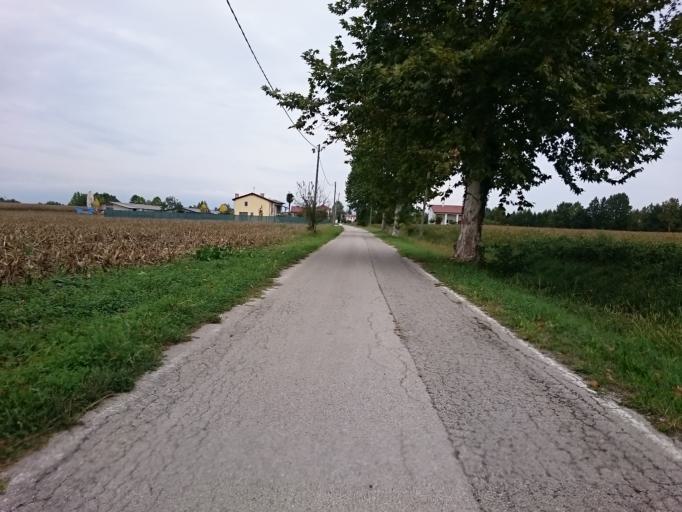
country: IT
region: Veneto
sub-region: Provincia di Vicenza
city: Quinto Vicentino
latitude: 45.5602
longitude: 11.6587
